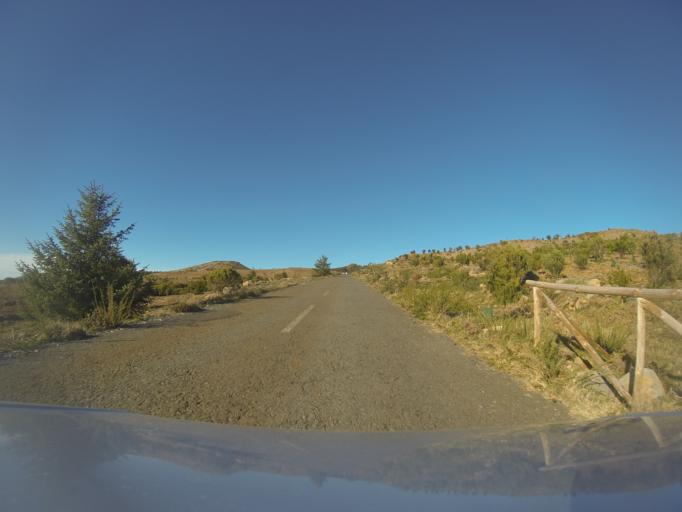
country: PT
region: Madeira
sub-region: Sao Vicente
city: Sao Vicente
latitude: 32.7678
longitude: -17.0799
